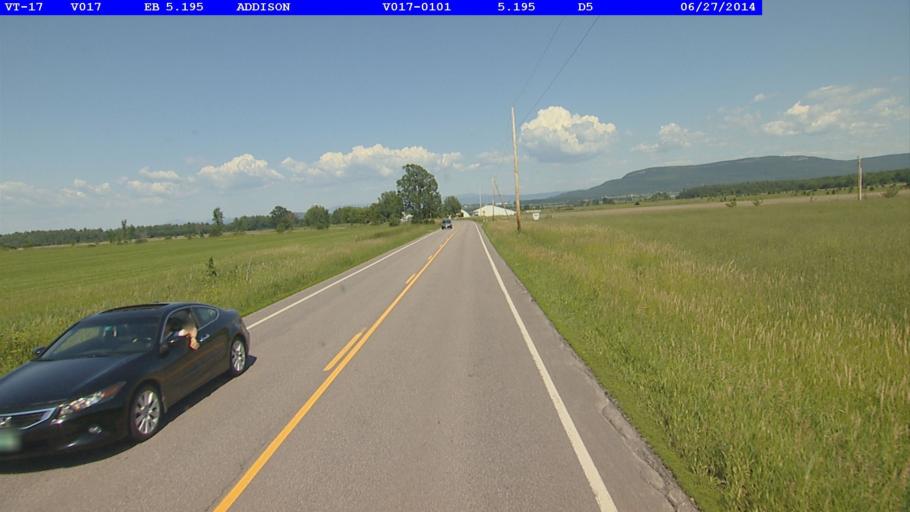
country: US
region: New York
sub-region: Essex County
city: Port Henry
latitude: 44.0821
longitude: -73.3651
